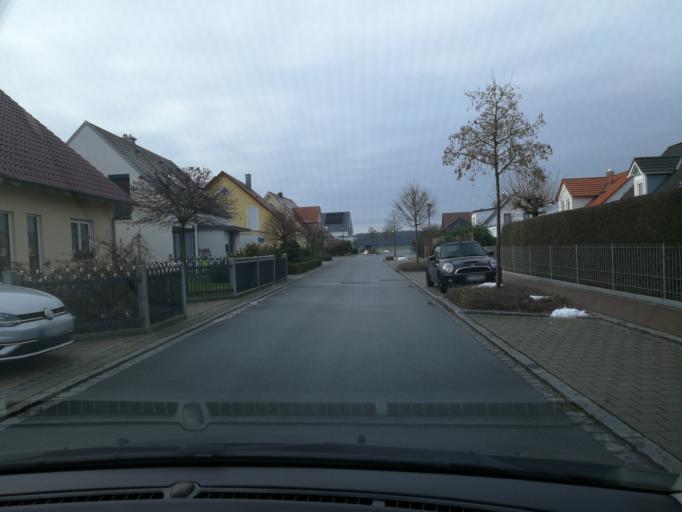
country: DE
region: Bavaria
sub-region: Regierungsbezirk Mittelfranken
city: Obermichelbach
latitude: 49.5278
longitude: 10.9053
